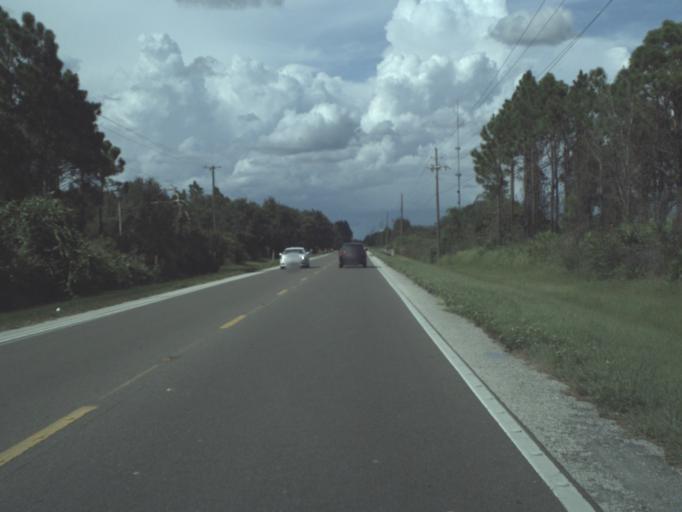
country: US
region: Florida
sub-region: Hardee County
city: Zolfo Springs
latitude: 27.3592
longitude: -81.8003
